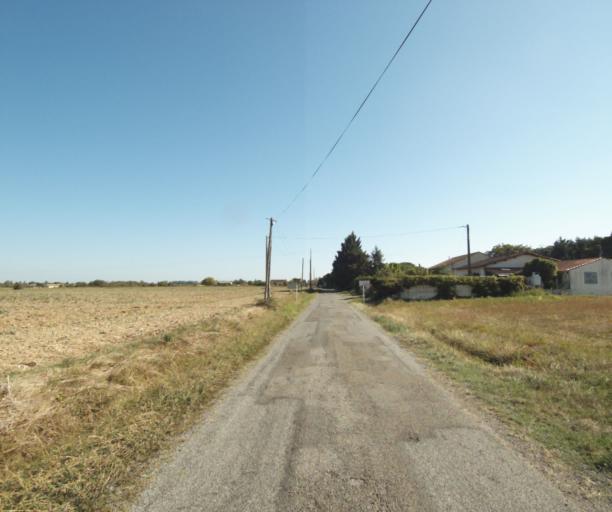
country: FR
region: Midi-Pyrenees
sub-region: Departement du Tarn-et-Garonne
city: Verdun-sur-Garonne
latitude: 43.8392
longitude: 1.2261
